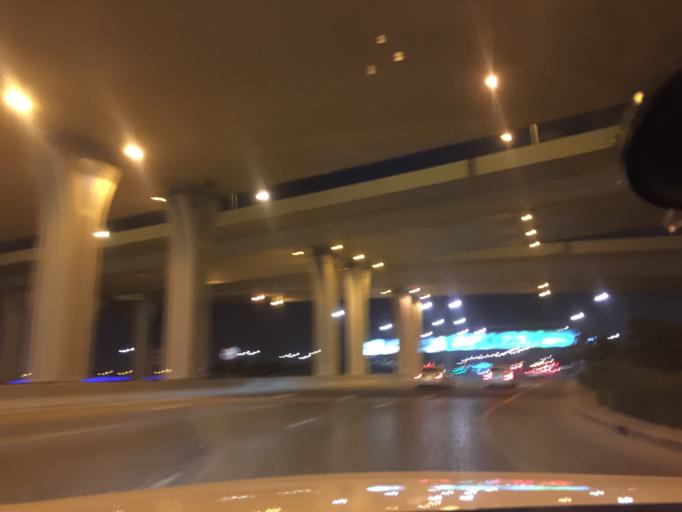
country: AE
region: Ash Shariqah
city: Sharjah
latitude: 25.2282
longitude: 55.3505
